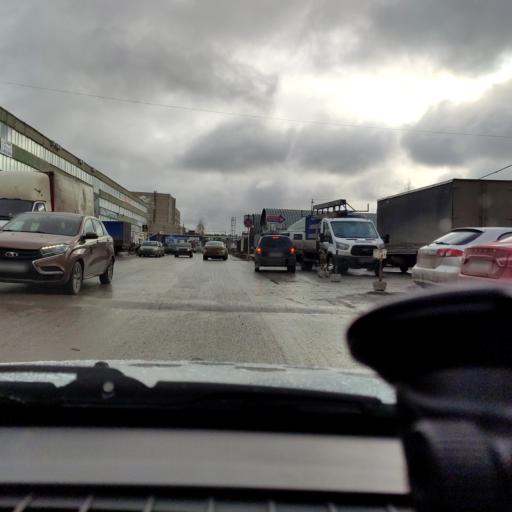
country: RU
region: Perm
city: Froly
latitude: 57.9600
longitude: 56.2747
